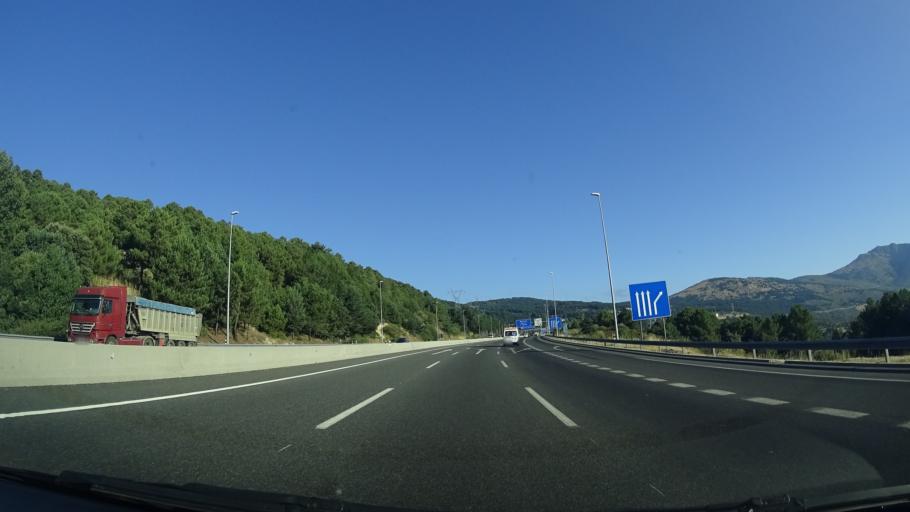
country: ES
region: Madrid
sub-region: Provincia de Madrid
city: Guadarrama
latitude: 40.6889
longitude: -4.1213
